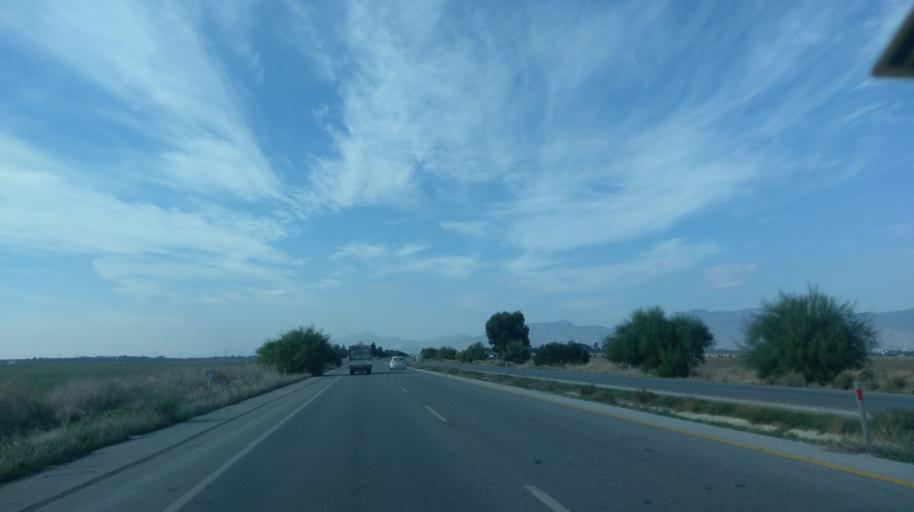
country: CY
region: Ammochostos
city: Lefkonoiko
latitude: 35.1911
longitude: 33.6256
